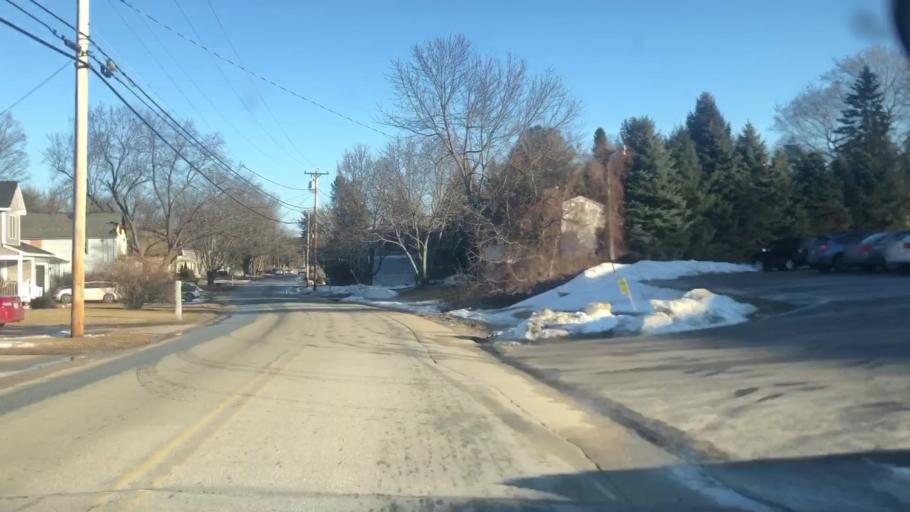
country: US
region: New Hampshire
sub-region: Hillsborough County
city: Milford
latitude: 42.8351
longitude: -71.6626
